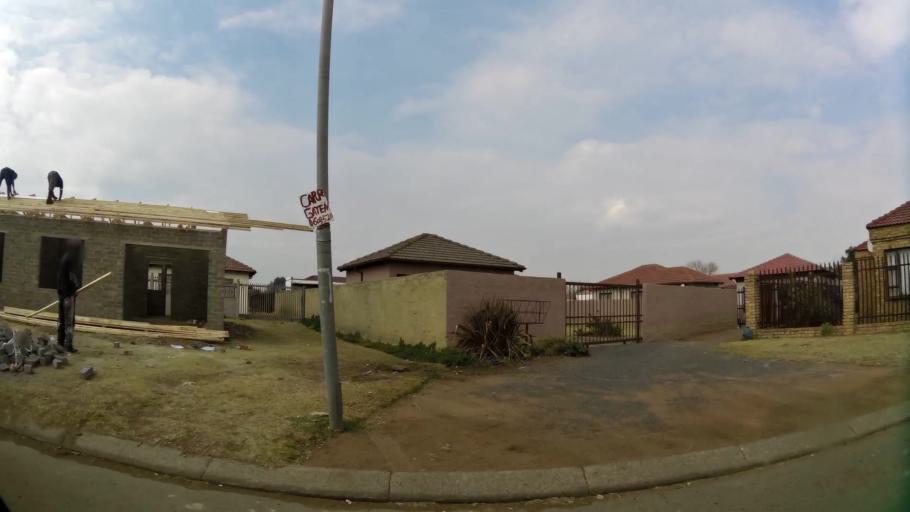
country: ZA
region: Gauteng
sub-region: Sedibeng District Municipality
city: Vanderbijlpark
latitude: -26.6855
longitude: 27.8435
